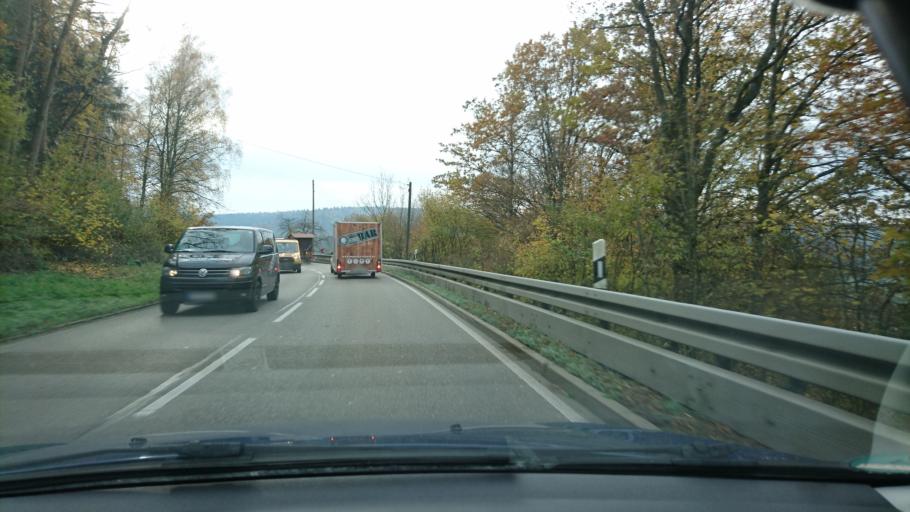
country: DE
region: Baden-Wuerttemberg
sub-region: Regierungsbezirk Stuttgart
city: Urbach
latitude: 48.8420
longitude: 9.5481
